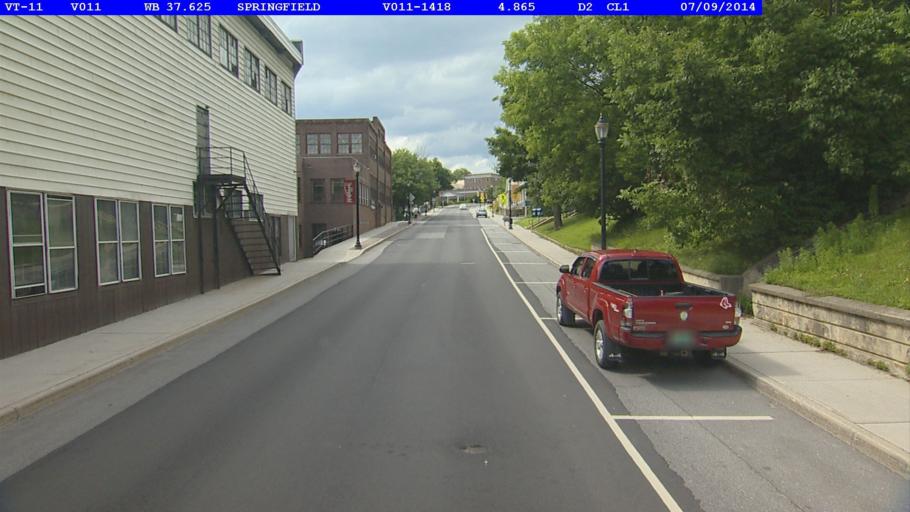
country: US
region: Vermont
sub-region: Windsor County
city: Springfield
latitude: 43.2955
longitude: -72.4804
